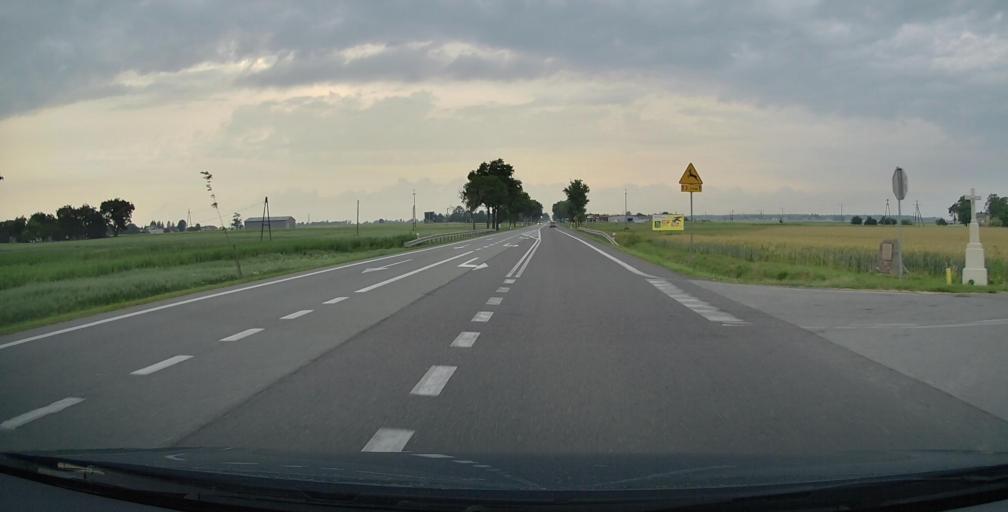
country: PL
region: Masovian Voivodeship
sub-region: Powiat siedlecki
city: Zbuczyn
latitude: 52.1038
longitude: 22.3970
